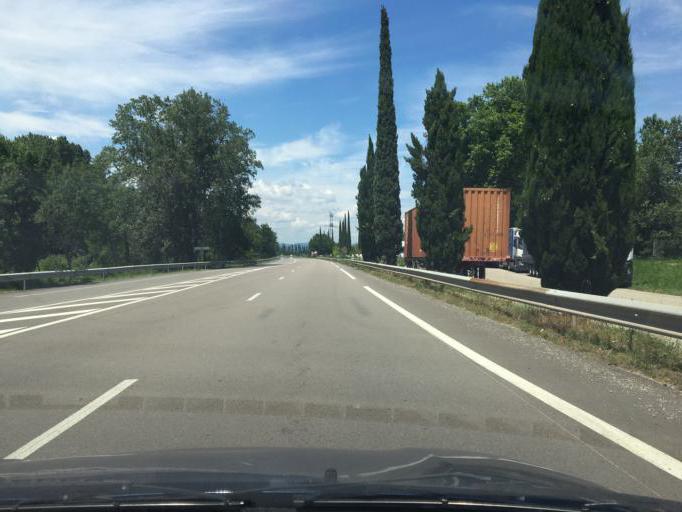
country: FR
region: Rhone-Alpes
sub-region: Departement de la Drome
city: Saulce-sur-Rhone
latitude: 44.6758
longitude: 4.7950
